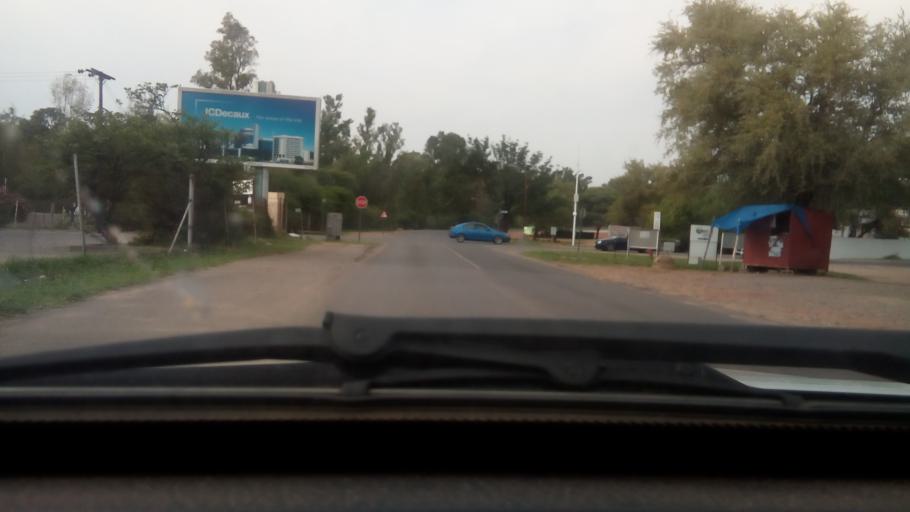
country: BW
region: South East
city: Gaborone
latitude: -24.6685
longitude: 25.9415
